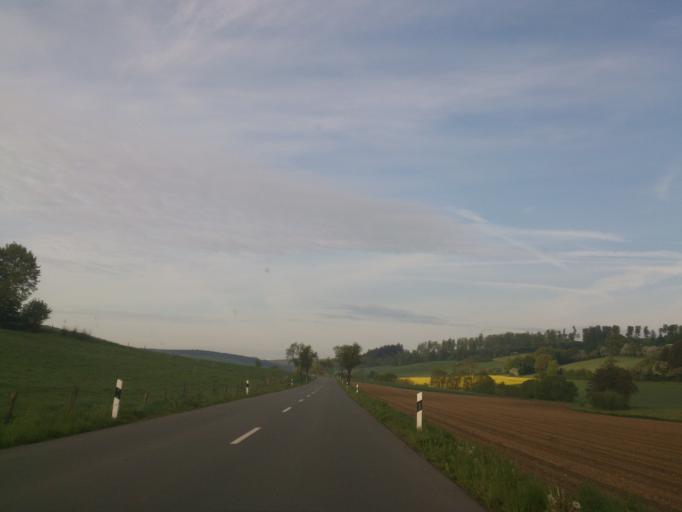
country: DE
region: North Rhine-Westphalia
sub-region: Regierungsbezirk Detmold
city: Altenbeken
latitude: 51.7093
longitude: 8.9048
